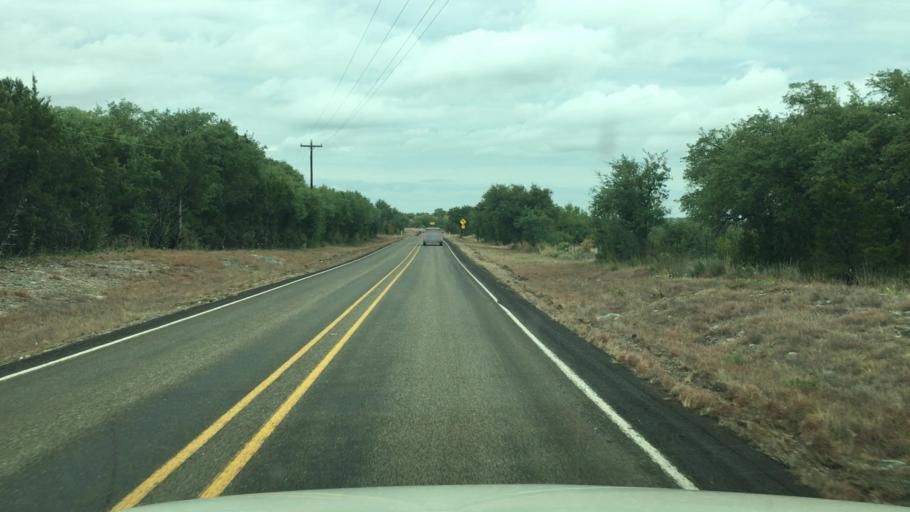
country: US
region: Texas
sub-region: Llano County
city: Horseshoe Bay
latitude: 30.4736
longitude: -98.4159
